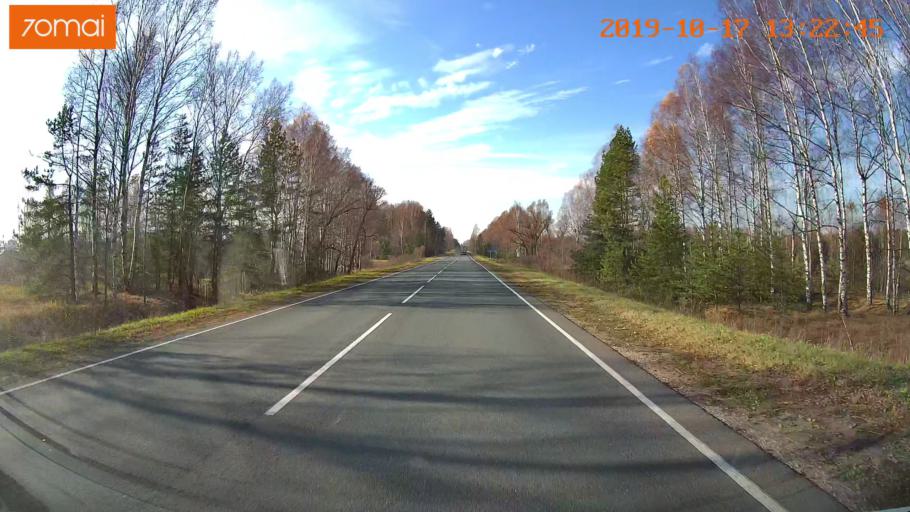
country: RU
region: Rjazan
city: Gus'-Zheleznyy
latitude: 55.0869
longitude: 40.9950
